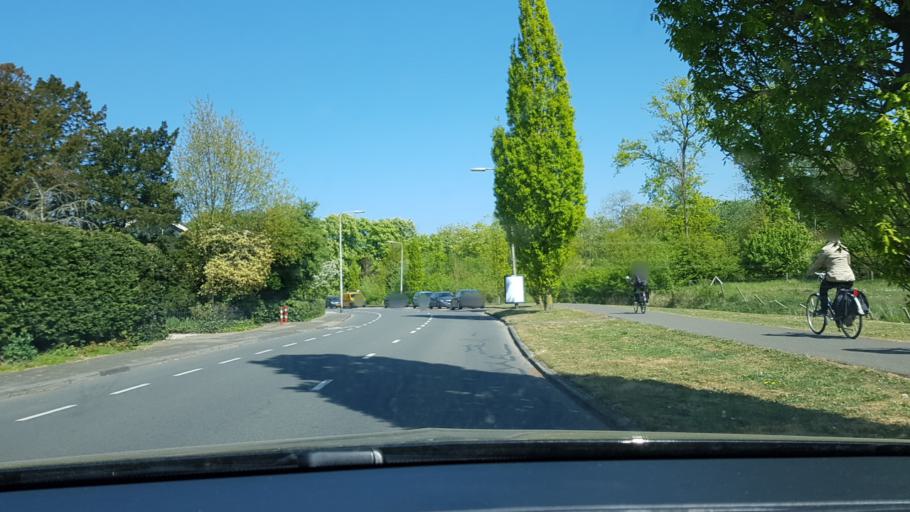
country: NL
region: North Holland
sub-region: Gemeente Bloemendaal
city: Bennebroek
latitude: 52.3237
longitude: 4.6025
